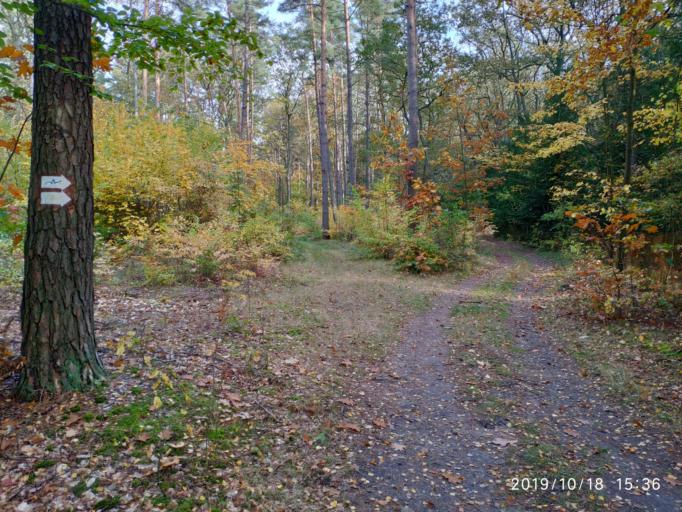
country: PL
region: Lubusz
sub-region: Powiat zielonogorski
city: Ochla
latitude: 51.8930
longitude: 15.4716
